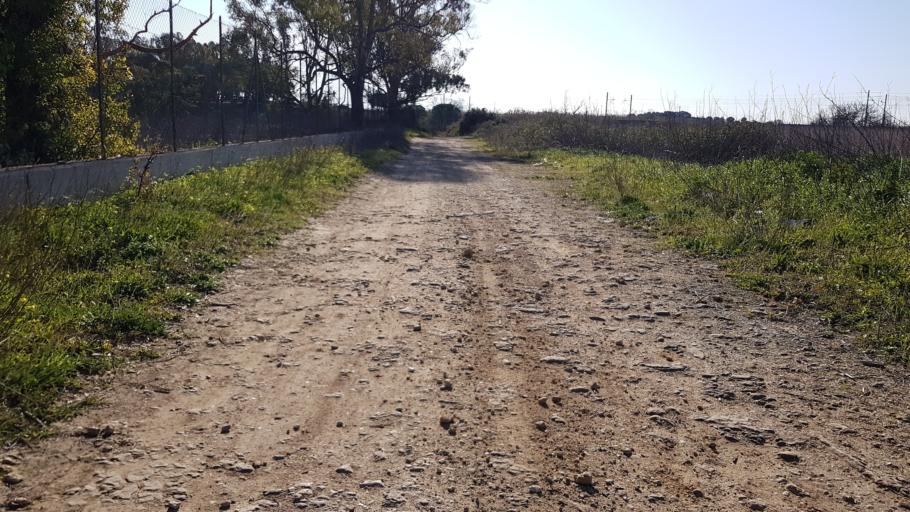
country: IT
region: Apulia
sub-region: Provincia di Brindisi
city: Brindisi
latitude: 40.6263
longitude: 17.8930
